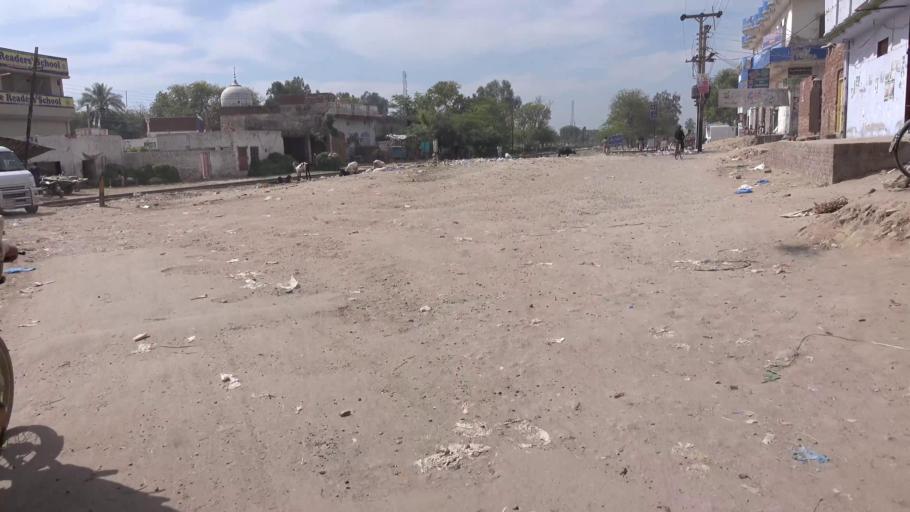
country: PK
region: Punjab
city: Hafizabad
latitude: 32.0668
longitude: 73.6852
